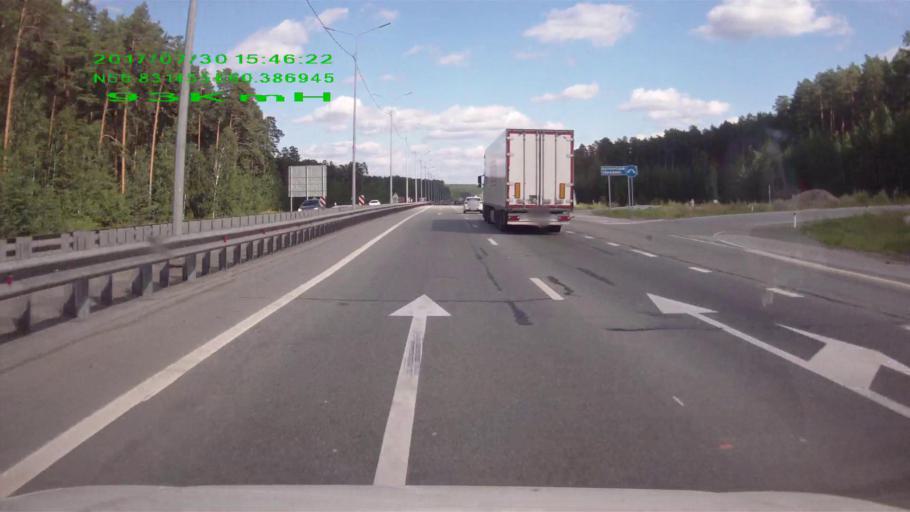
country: RU
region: Sverdlovsk
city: Severka
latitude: 56.8314
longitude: 60.3876
